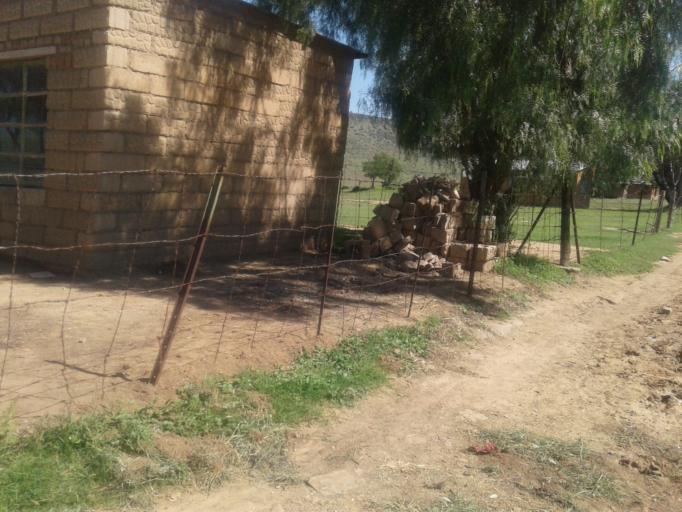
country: LS
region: Mafeteng
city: Mafeteng
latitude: -29.7520
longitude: 27.1078
